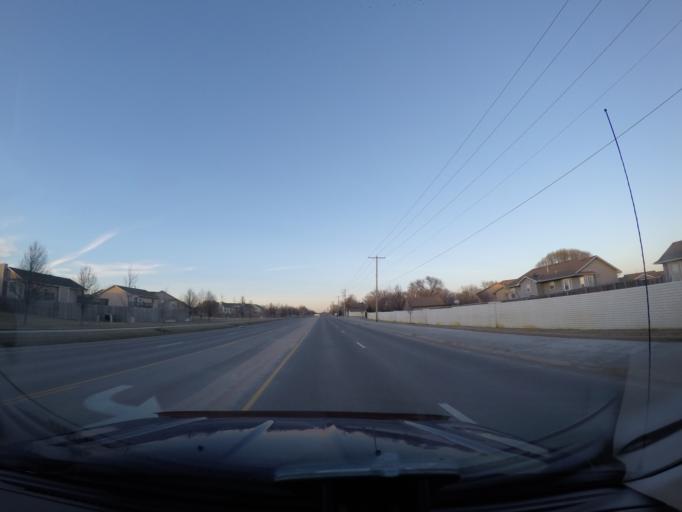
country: US
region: Kansas
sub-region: Sedgwick County
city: Goddard
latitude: 37.6533
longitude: -97.4808
